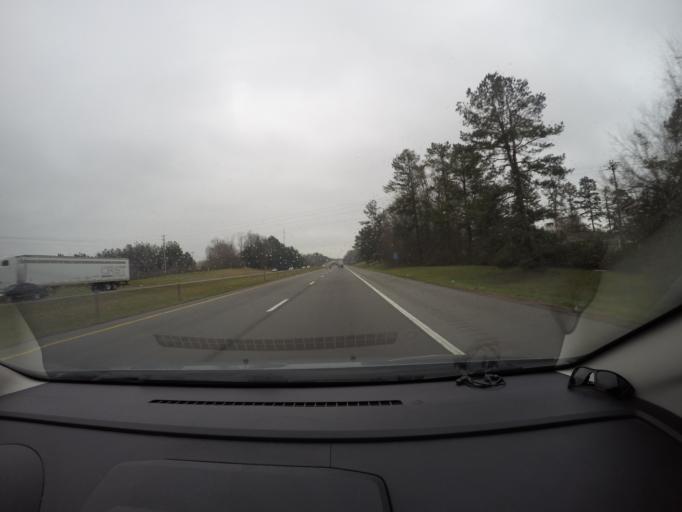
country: US
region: Tennessee
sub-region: Coffee County
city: Manchester
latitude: 35.4829
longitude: -86.0684
